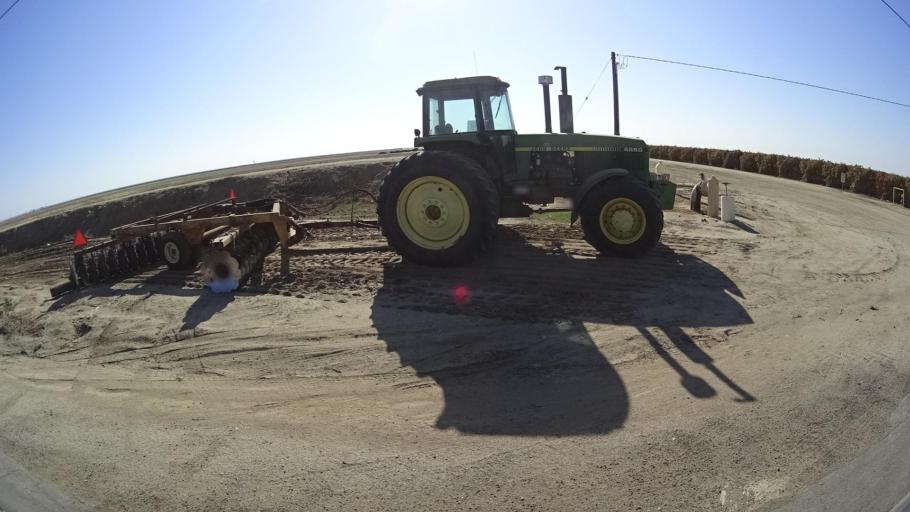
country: US
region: California
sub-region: Kern County
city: McFarland
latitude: 35.7179
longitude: -119.1781
